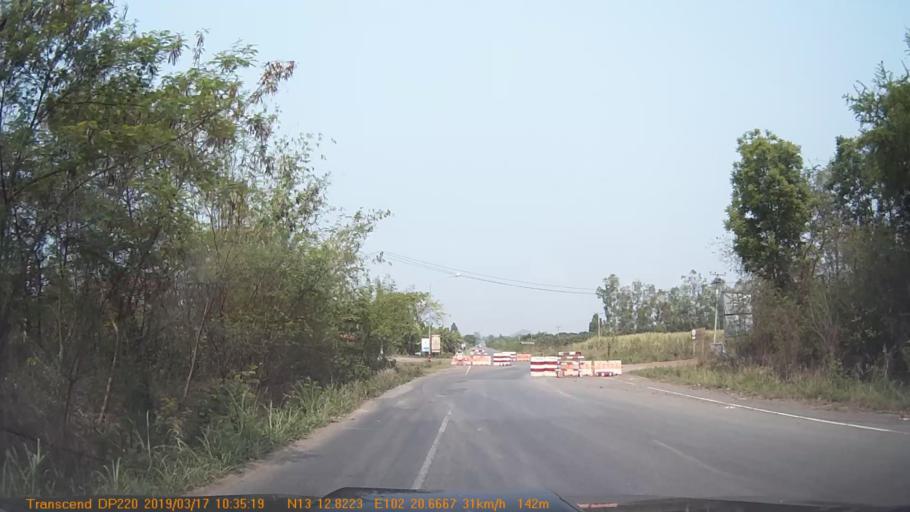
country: TH
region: Chanthaburi
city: Soi Dao
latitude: 13.2138
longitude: 102.3443
